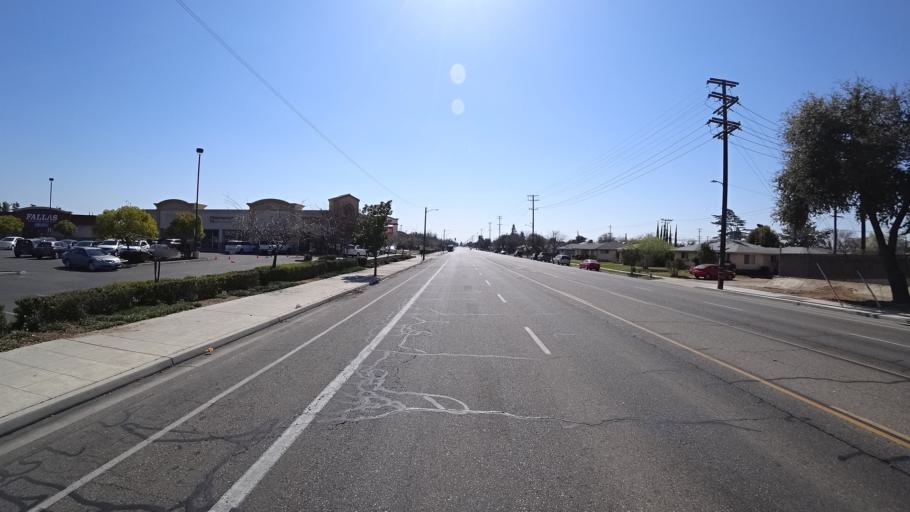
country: US
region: California
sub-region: Fresno County
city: Fresno
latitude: 36.7920
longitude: -119.8264
